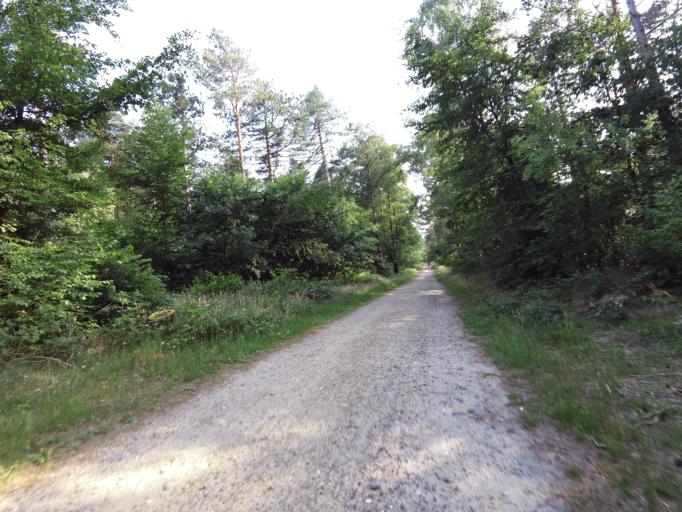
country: DE
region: Lower Saxony
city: Nordholz
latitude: 53.8451
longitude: 8.5913
